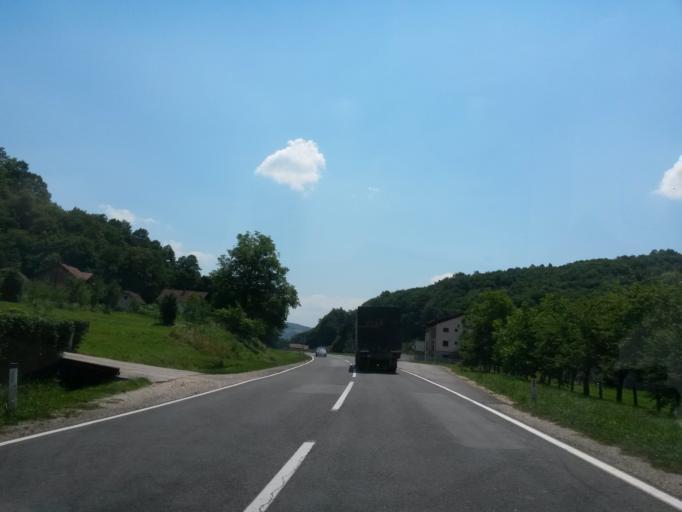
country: BA
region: Federation of Bosnia and Herzegovina
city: Lijesnica
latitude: 44.5027
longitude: 18.0794
